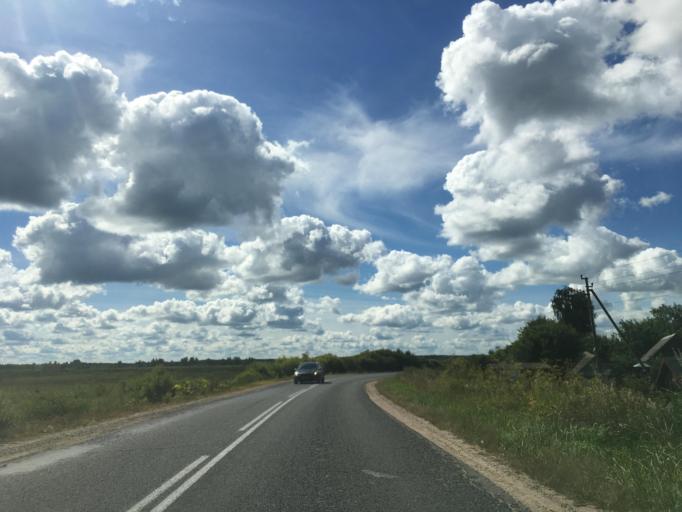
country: RU
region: Pskov
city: Pskov
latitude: 57.7426
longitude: 28.1581
